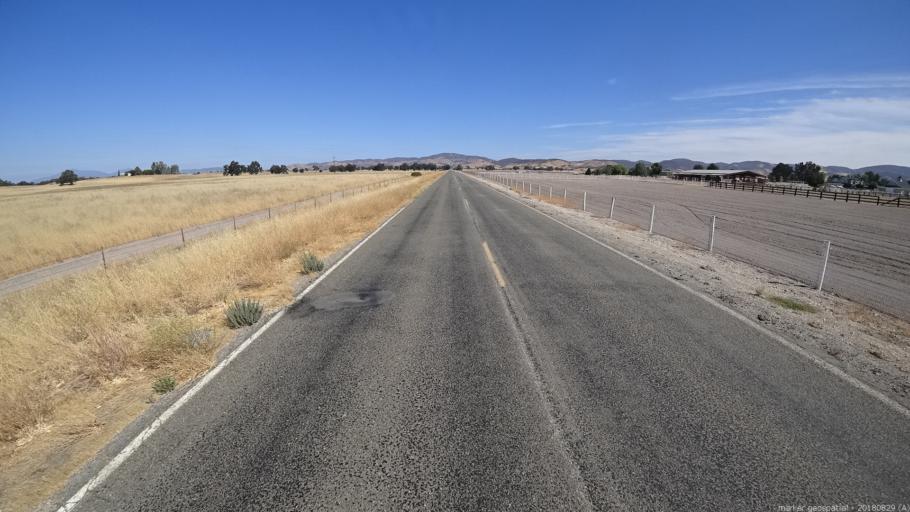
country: US
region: California
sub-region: San Luis Obispo County
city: Lake Nacimiento
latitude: 35.9263
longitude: -121.0822
